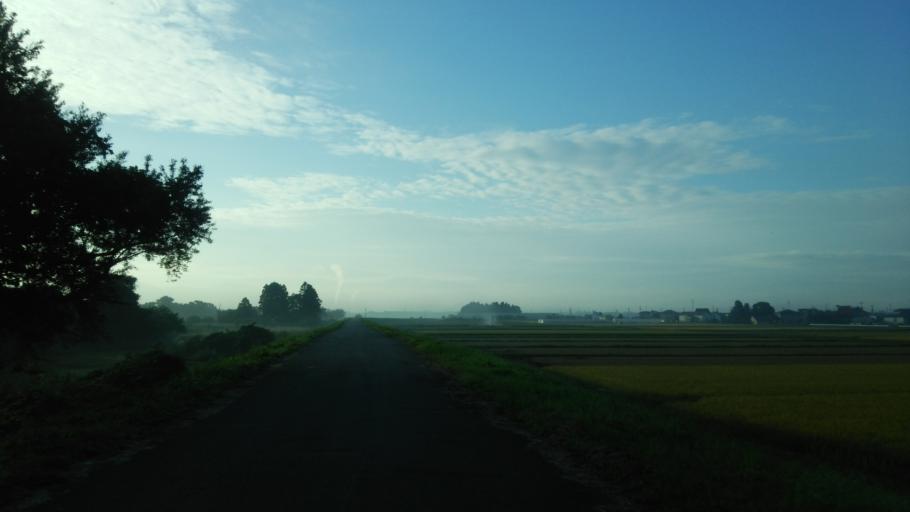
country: JP
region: Fukushima
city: Kitakata
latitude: 37.5442
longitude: 139.8621
